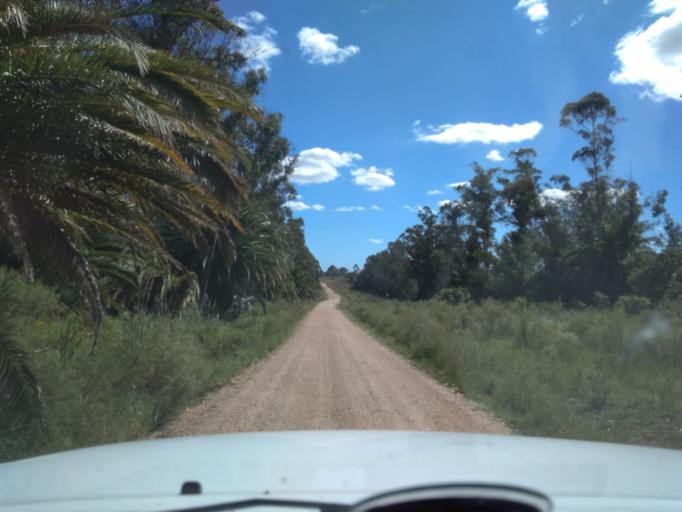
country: UY
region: Canelones
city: Joaquin Suarez
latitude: -34.7031
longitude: -56.0239
